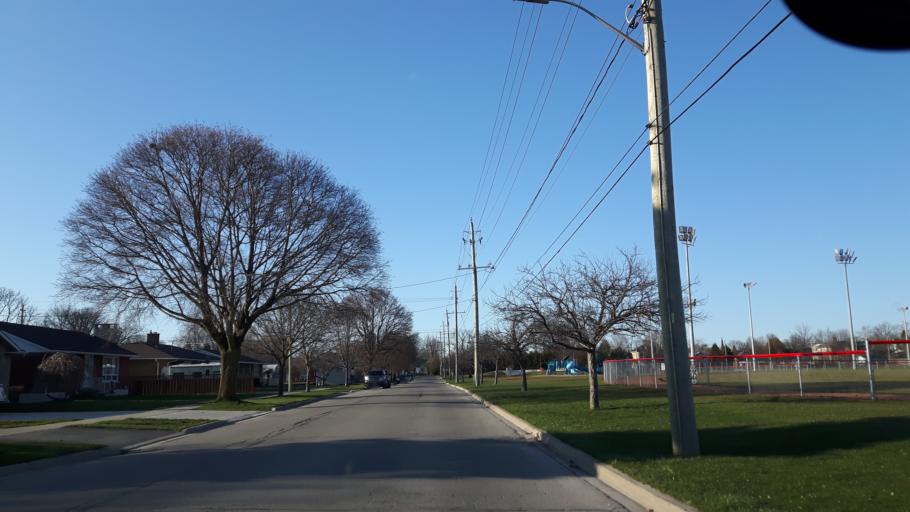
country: CA
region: Ontario
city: Goderich
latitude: 43.7363
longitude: -81.7163
